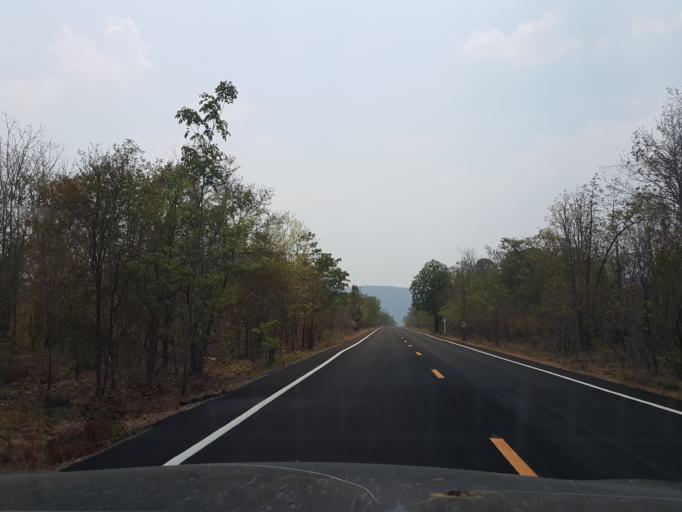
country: TH
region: Lampang
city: Mae Phrik
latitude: 17.4883
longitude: 99.1007
